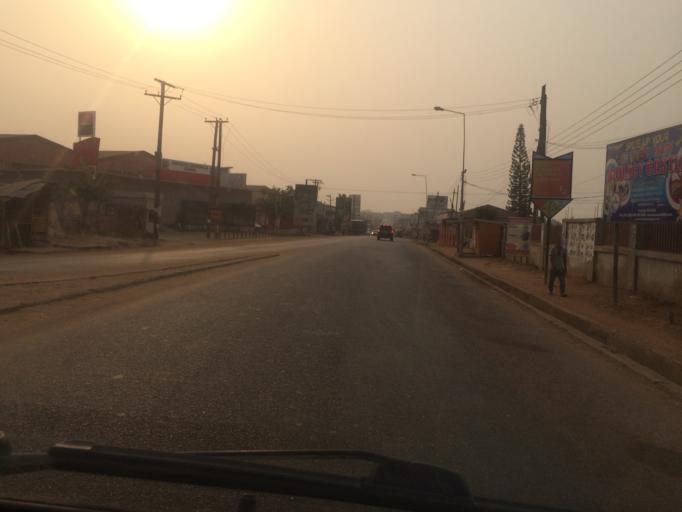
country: GH
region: Greater Accra
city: Nungua
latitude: 5.6435
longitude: -0.1111
